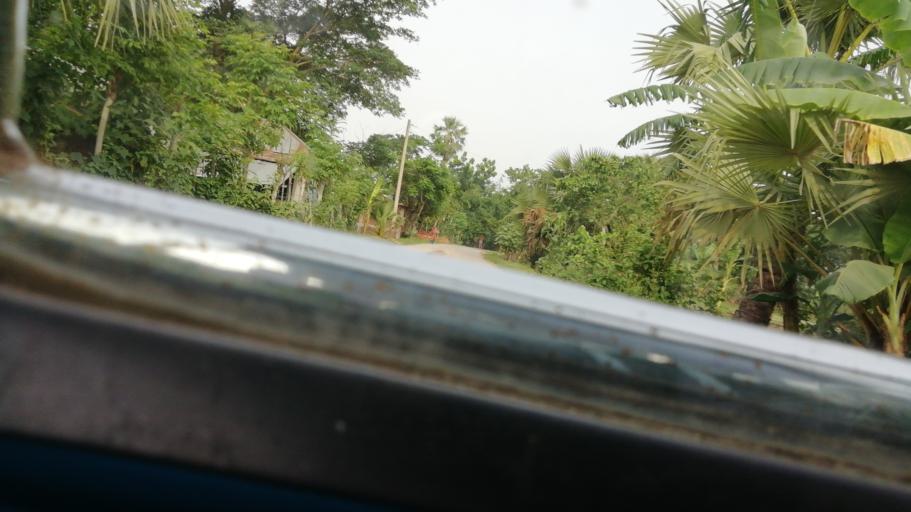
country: BD
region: Khulna
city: Bhatpara Abhaynagar
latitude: 23.0362
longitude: 89.3012
